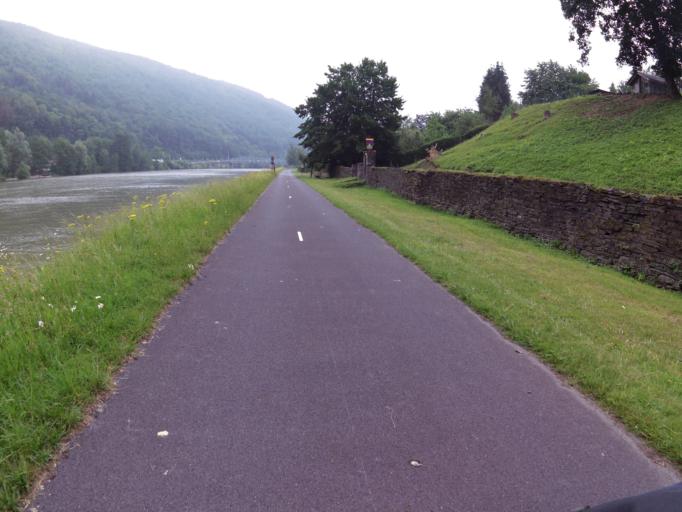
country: FR
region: Champagne-Ardenne
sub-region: Departement des Ardennes
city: Haybes
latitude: 50.0092
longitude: 4.7001
